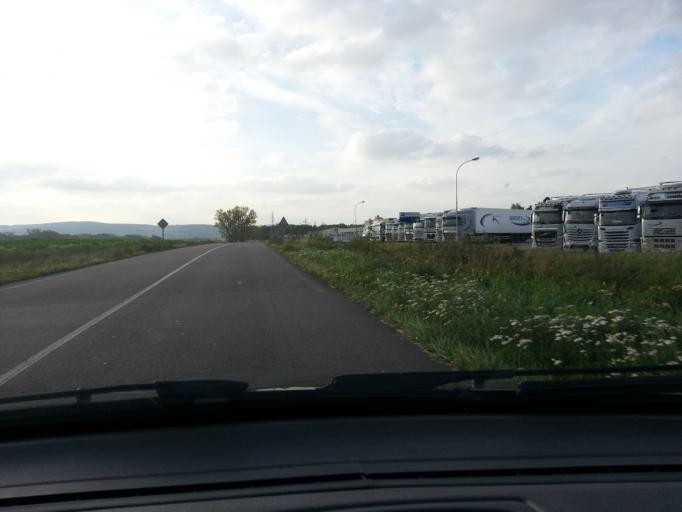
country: FR
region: Bourgogne
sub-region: Departement de Saone-et-Loire
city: Chatenoy-le-Royal
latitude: 46.7796
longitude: 4.7999
